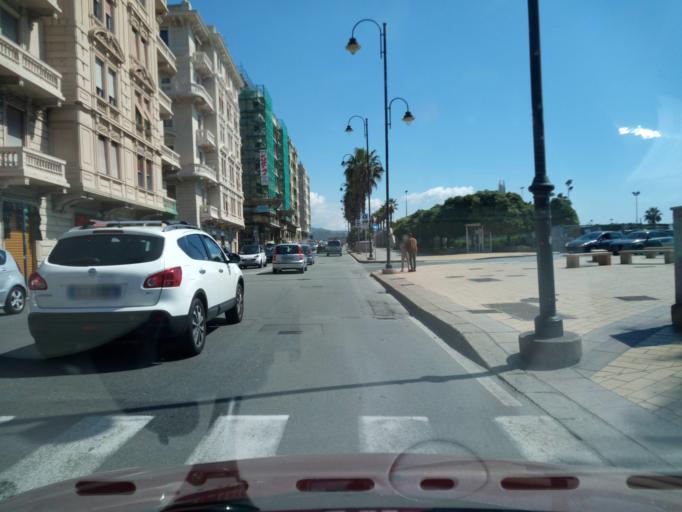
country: IT
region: Liguria
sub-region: Provincia di Genova
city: Mele
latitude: 44.4247
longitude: 8.8194
